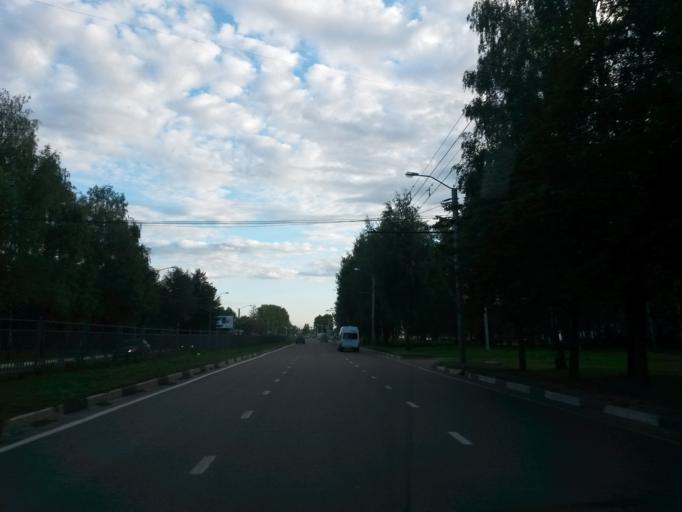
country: RU
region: Jaroslavl
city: Yaroslavl
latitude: 57.6770
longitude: 39.7759
